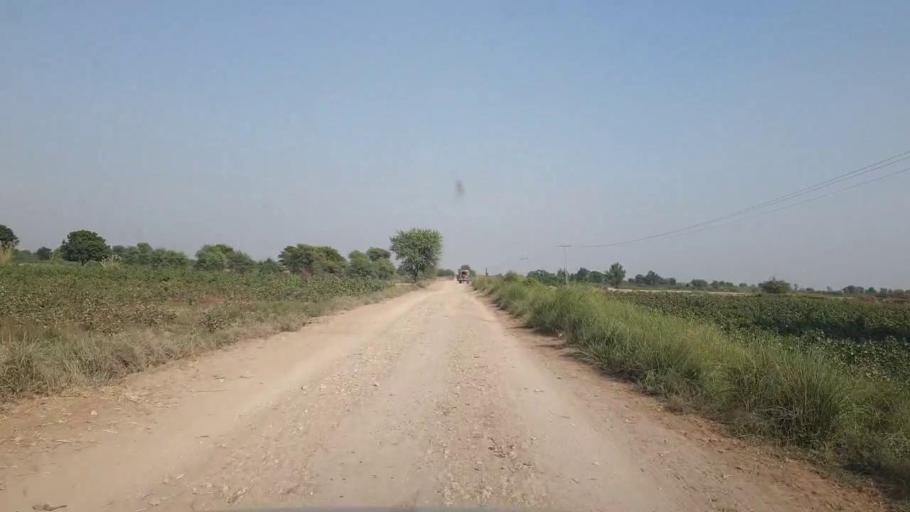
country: PK
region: Sindh
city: Sinjhoro
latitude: 26.0559
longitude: 68.8551
